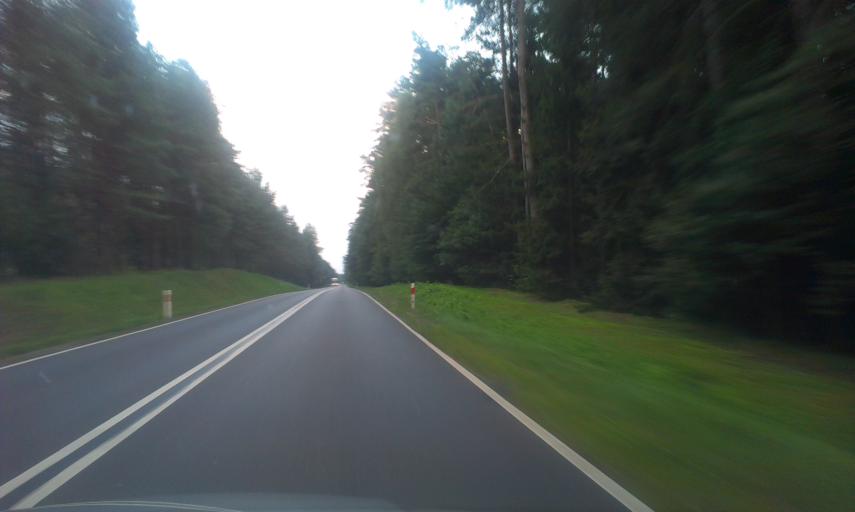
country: PL
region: West Pomeranian Voivodeship
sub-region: Powiat koszalinski
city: Sianow
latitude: 54.0879
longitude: 16.3742
